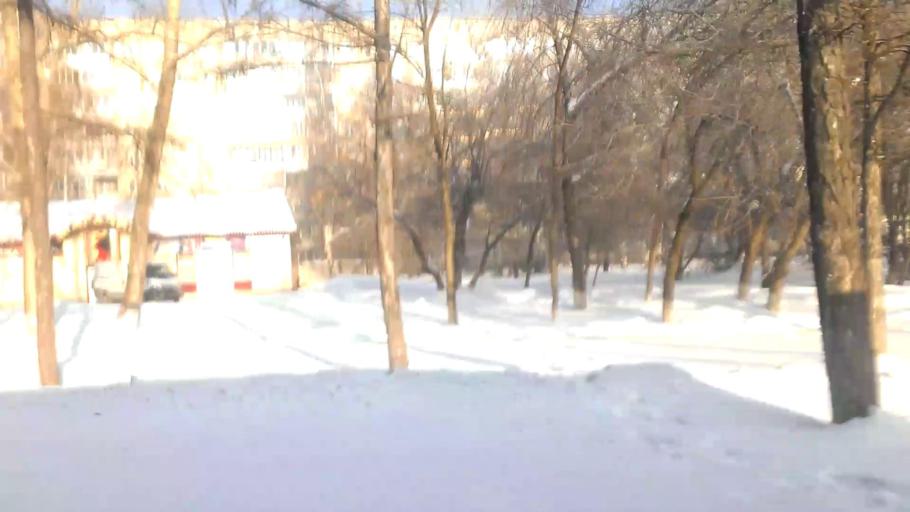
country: RU
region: Altai Krai
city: Novosilikatnyy
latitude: 53.3717
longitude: 83.6757
